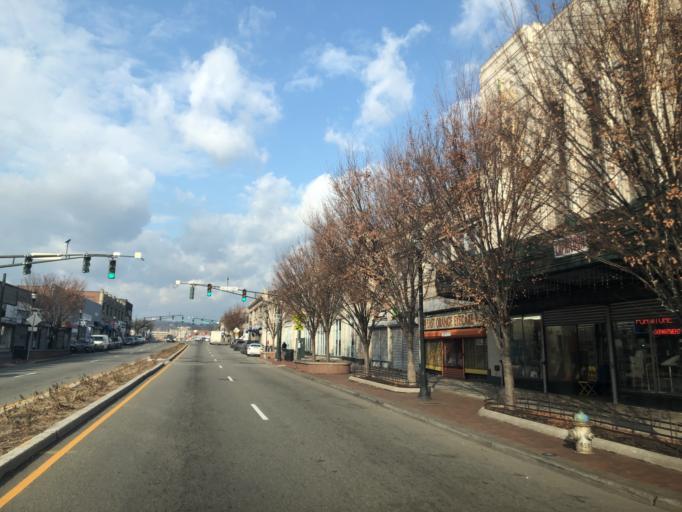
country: US
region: New Jersey
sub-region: Essex County
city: Orange
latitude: 40.7610
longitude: -74.2239
